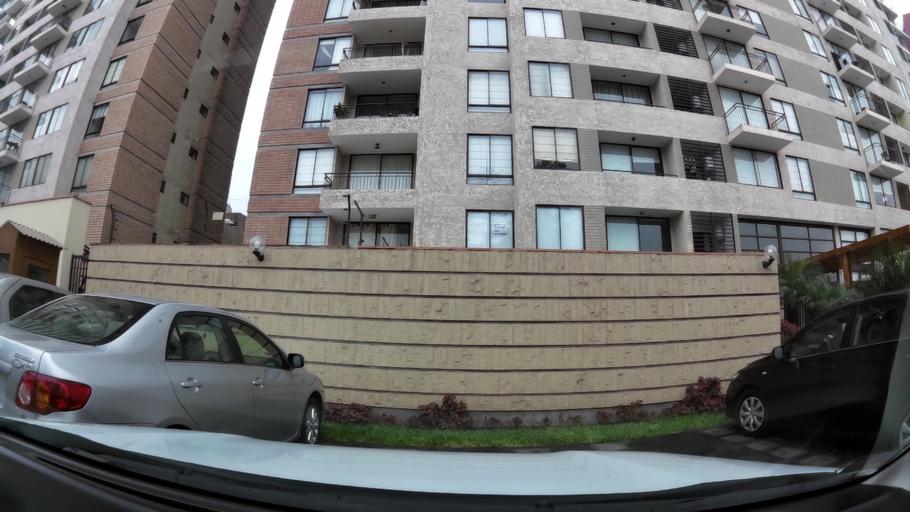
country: PE
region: Lima
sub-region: Lima
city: Surco
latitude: -12.1288
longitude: -77.0244
